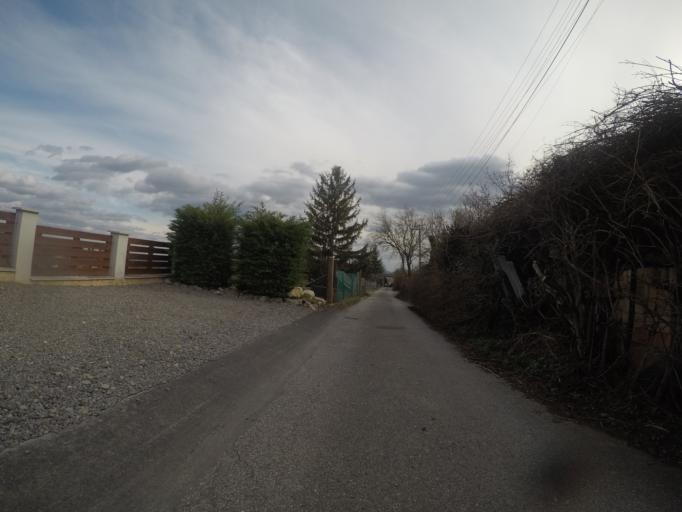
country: HU
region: Baranya
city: Pecs
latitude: 46.0910
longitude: 18.2009
